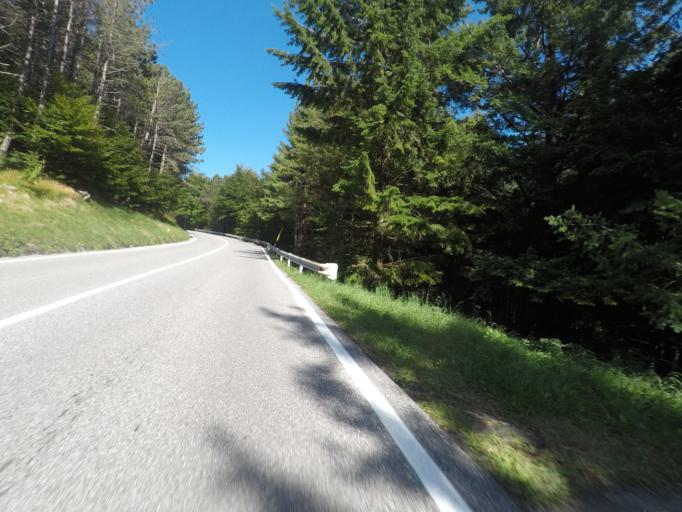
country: IT
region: Emilia-Romagna
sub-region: Provincia di Reggio Emilia
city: Collagna
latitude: 44.3024
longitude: 10.2151
